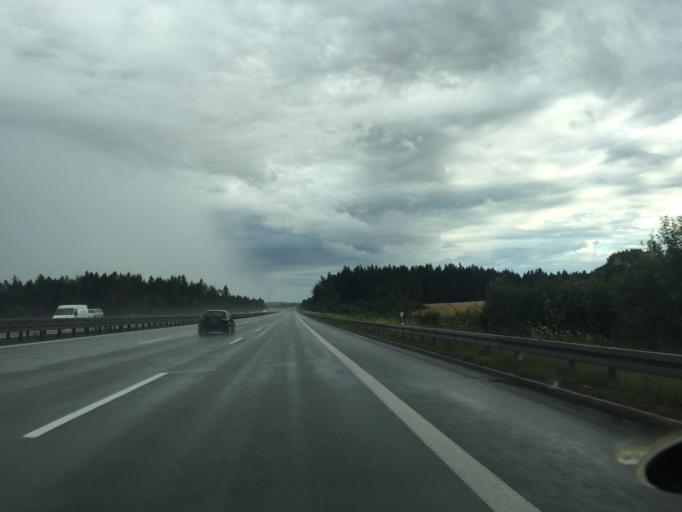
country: DE
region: Bavaria
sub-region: Upper Franconia
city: Leupoldsgrun
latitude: 50.2730
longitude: 11.8060
